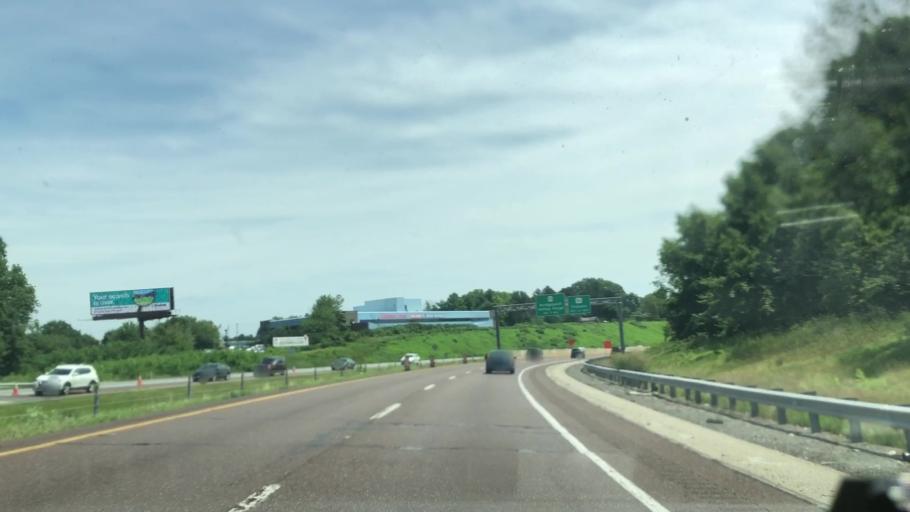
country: US
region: Pennsylvania
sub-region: Montgomery County
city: Audubon
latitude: 40.1163
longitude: -75.4268
